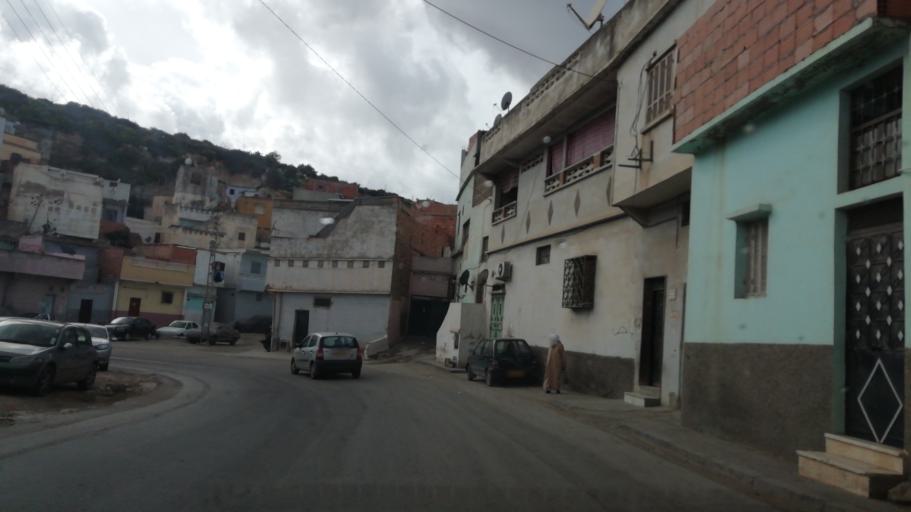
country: DZ
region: Oran
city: Oran
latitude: 35.6968
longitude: -0.6612
